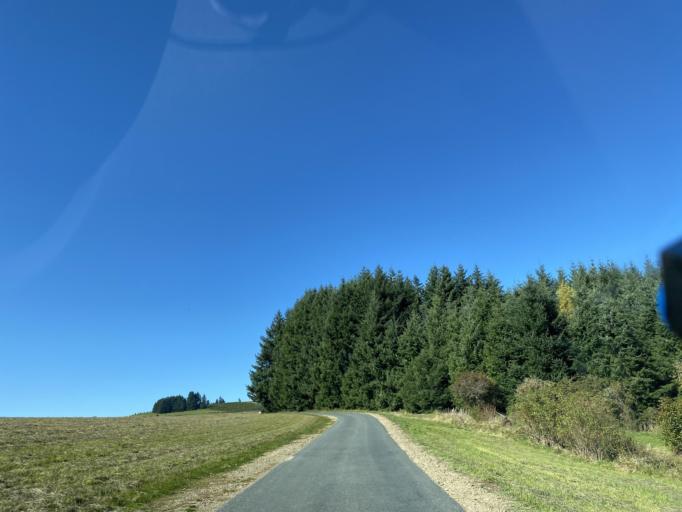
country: FR
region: Rhone-Alpes
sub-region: Departement de la Loire
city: Saint-Just-en-Chevalet
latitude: 45.9609
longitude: 3.8750
